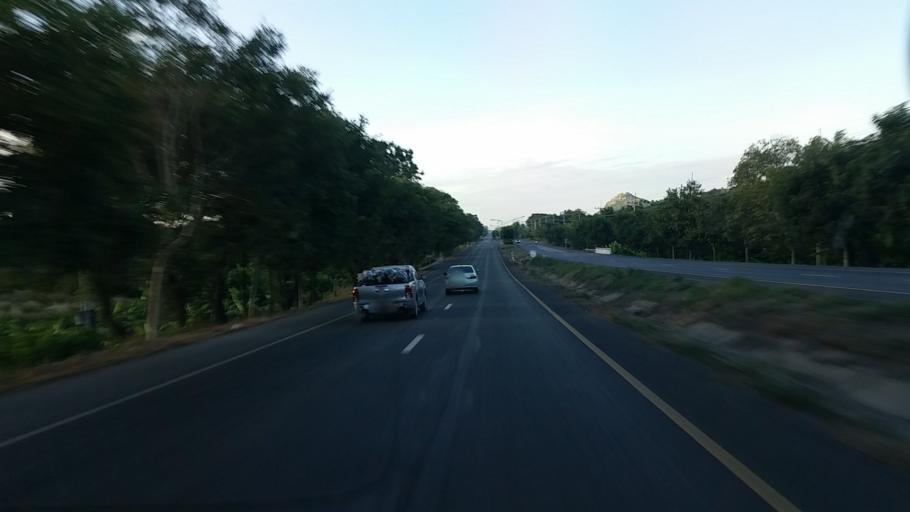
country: TH
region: Lop Buri
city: Chai Badan
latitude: 15.1528
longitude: 101.0541
